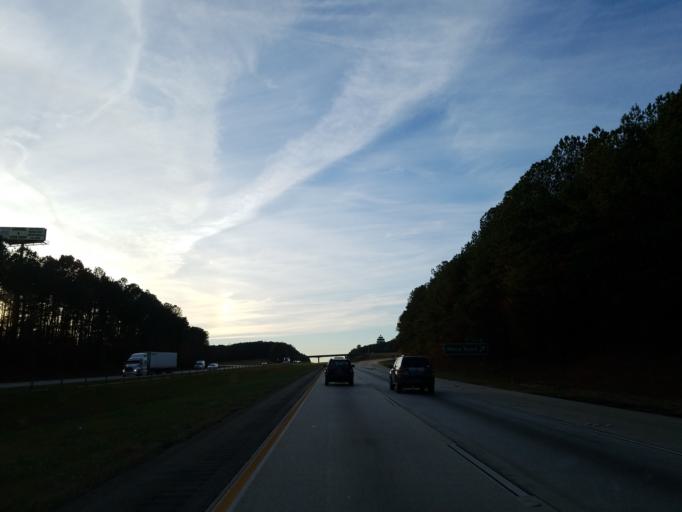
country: US
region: Georgia
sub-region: Haralson County
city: Bremen
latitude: 33.6888
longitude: -85.1818
